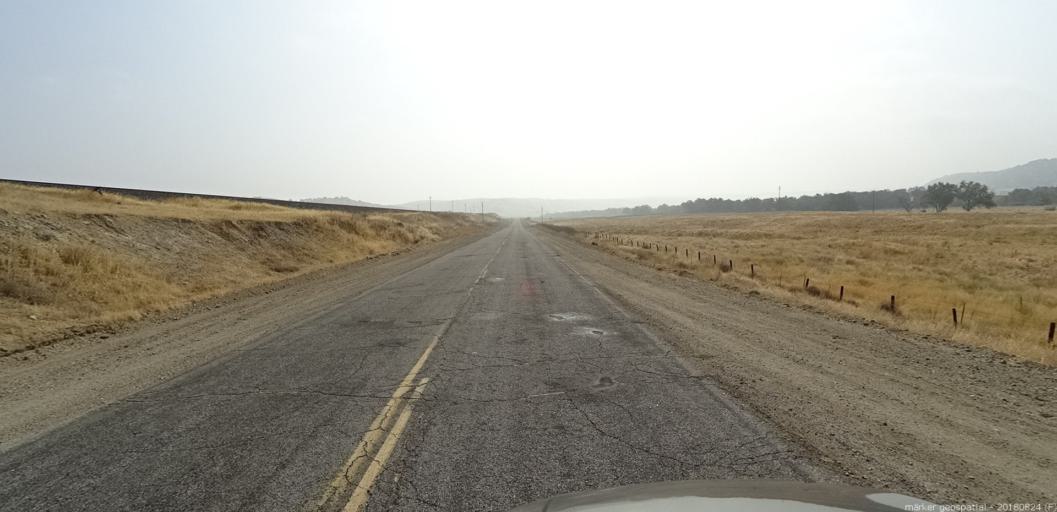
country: US
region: California
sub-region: San Luis Obispo County
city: San Miguel
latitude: 35.8622
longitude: -120.7900
